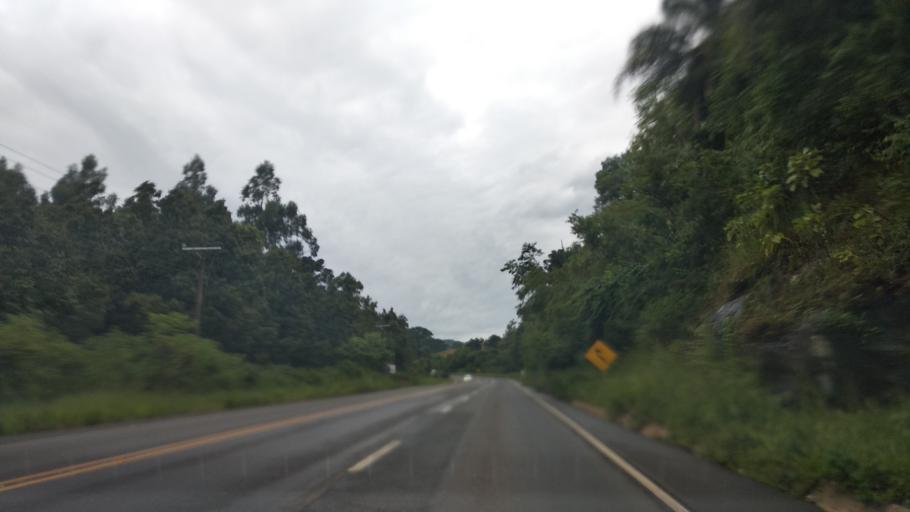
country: BR
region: Santa Catarina
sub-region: Videira
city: Videira
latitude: -27.0729
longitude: -51.2349
